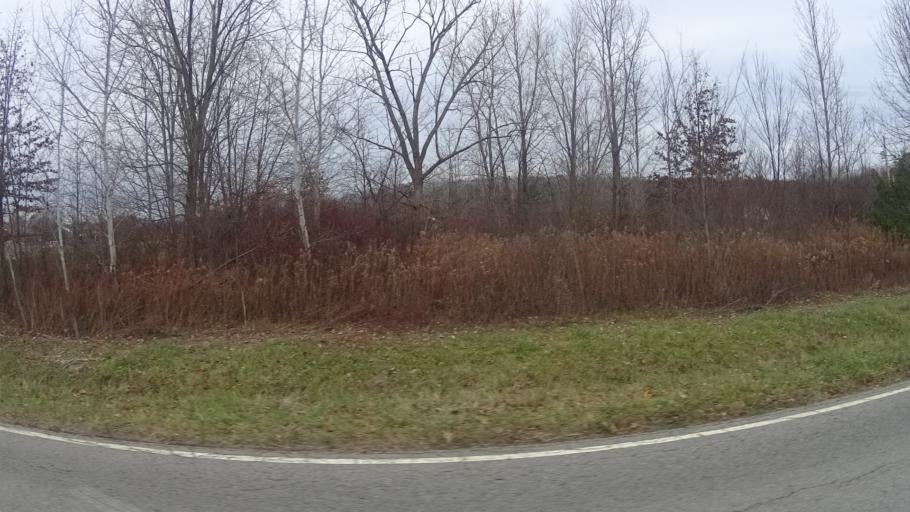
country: US
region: Ohio
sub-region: Cuyahoga County
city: Strongsville
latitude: 41.2894
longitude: -81.8953
